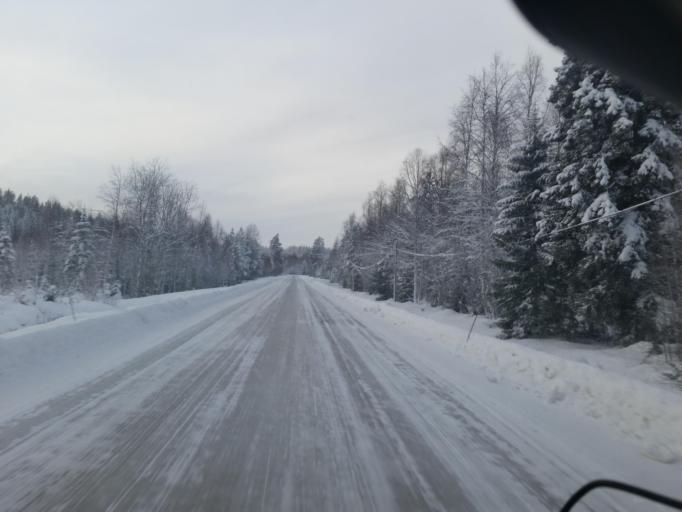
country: SE
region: Norrbotten
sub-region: Pitea Kommun
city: Norrfjarden
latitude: 65.5212
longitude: 21.4487
